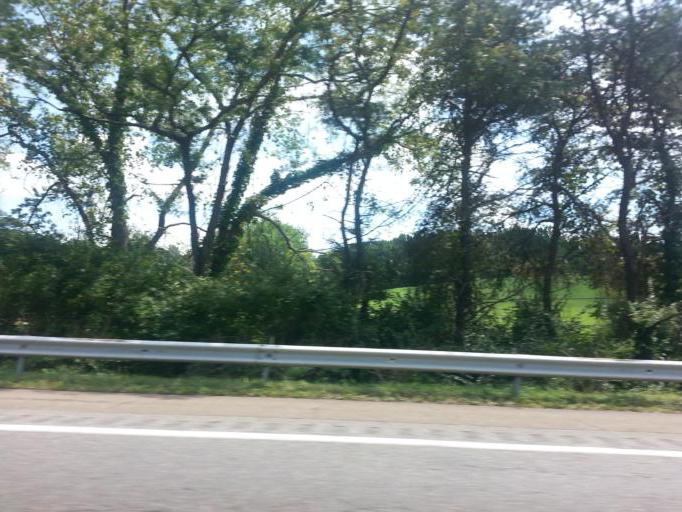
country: US
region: Tennessee
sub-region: Sullivan County
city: Fairmount
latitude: 36.6404
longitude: -82.0971
